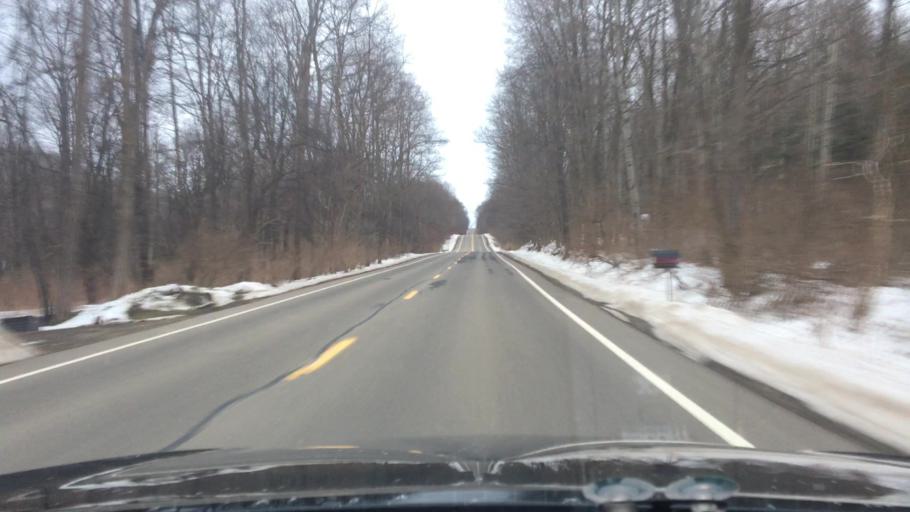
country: US
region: New York
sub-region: Chautauqua County
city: Lakewood
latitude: 42.1758
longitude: -79.3666
